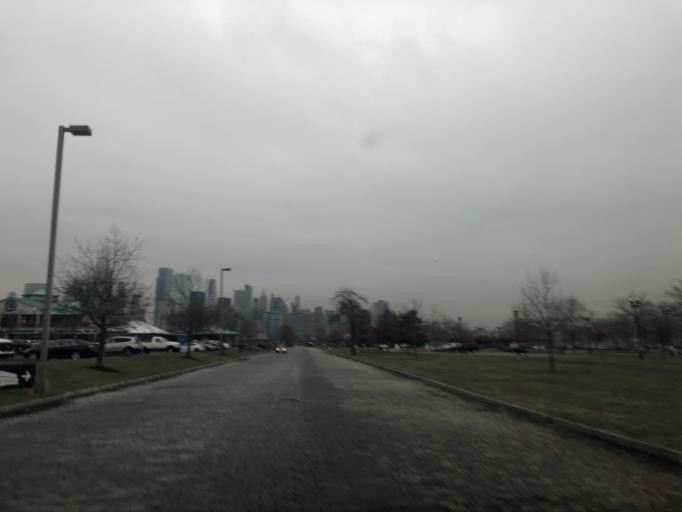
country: US
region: New York
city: New York City
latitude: 40.7088
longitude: -74.0420
